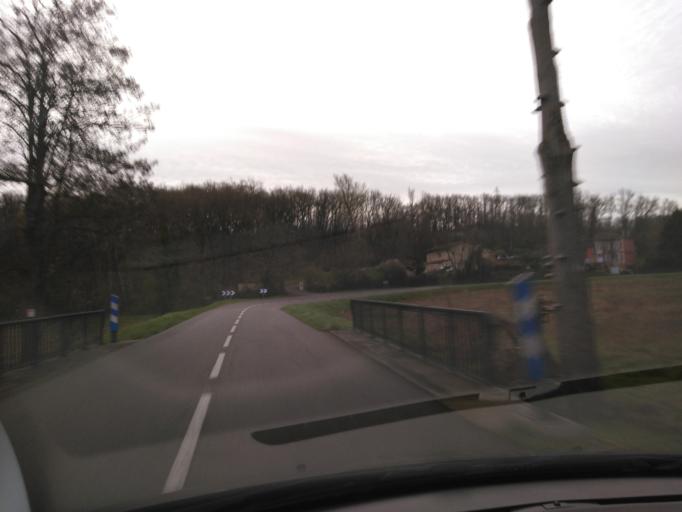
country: FR
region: Midi-Pyrenees
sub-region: Departement du Tarn-et-Garonne
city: Verdun-sur-Garonne
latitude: 43.8443
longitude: 1.1577
